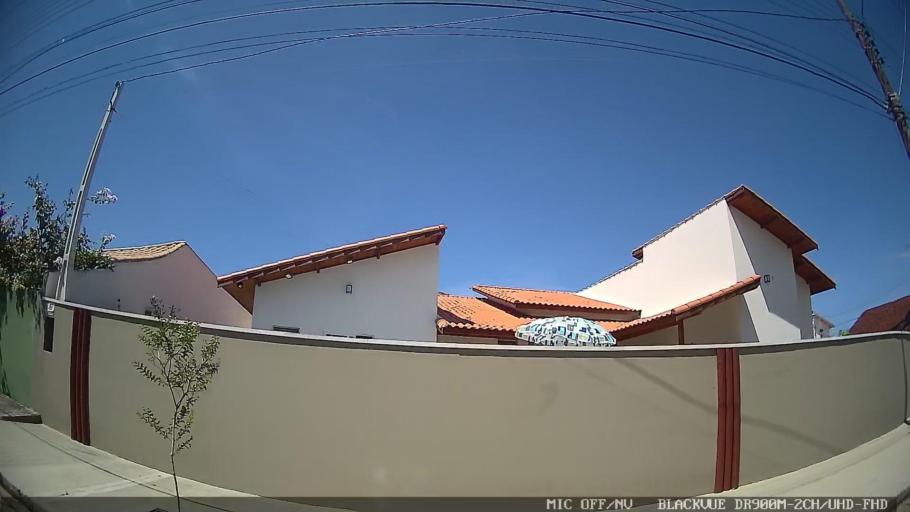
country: BR
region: Sao Paulo
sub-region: Peruibe
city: Peruibe
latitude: -24.2919
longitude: -46.9720
